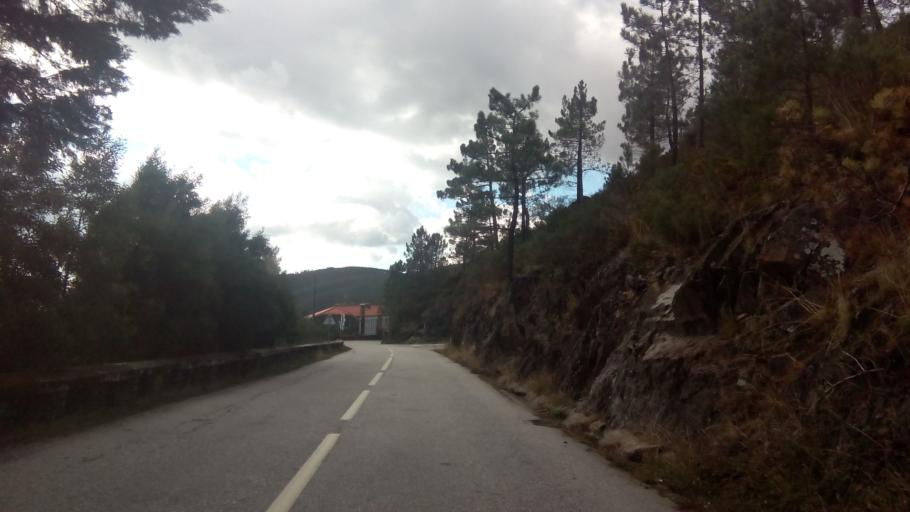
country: PT
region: Vila Real
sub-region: Mesao Frio
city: Mesao Frio
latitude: 41.2762
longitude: -7.9305
